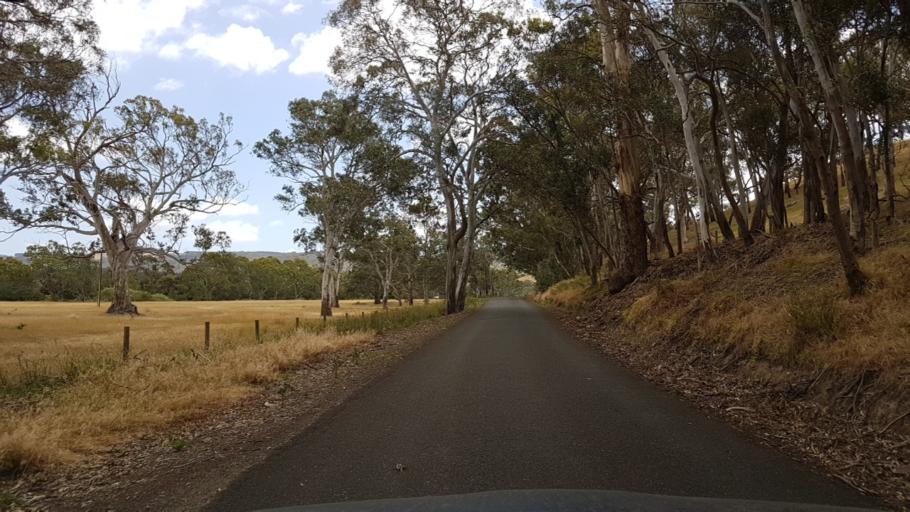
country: AU
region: South Australia
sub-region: Victor Harbor
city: Victor Harbor
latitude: -35.4737
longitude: 138.6011
